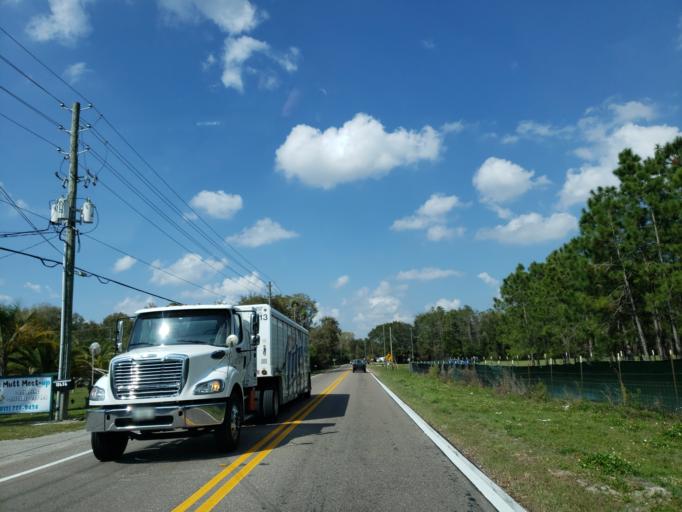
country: US
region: Florida
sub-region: Hillsborough County
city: Keystone
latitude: 28.1458
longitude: -82.5783
